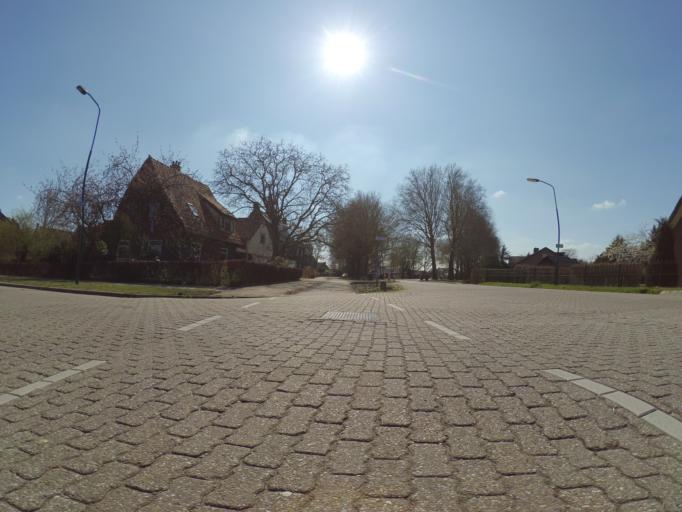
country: NL
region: Utrecht
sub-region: Gemeente Utrechtse Heuvelrug
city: Driebergen-Rijsenburg
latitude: 52.0267
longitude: 5.2440
